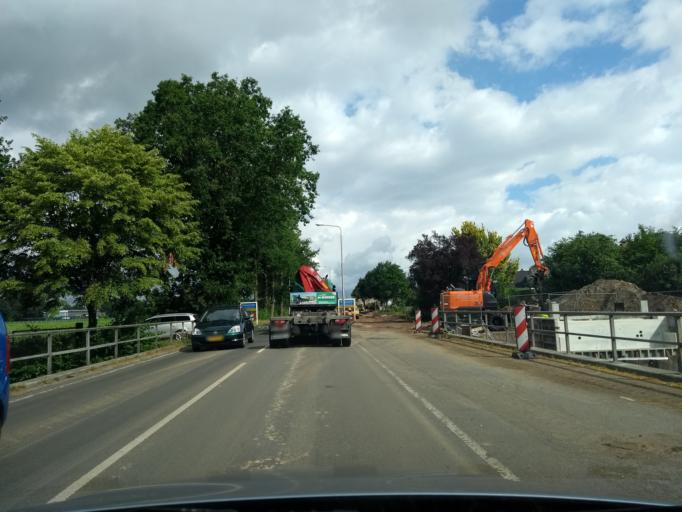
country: NL
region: Overijssel
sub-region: Gemeente Twenterand
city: Vriezenveen
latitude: 52.3975
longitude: 6.6100
